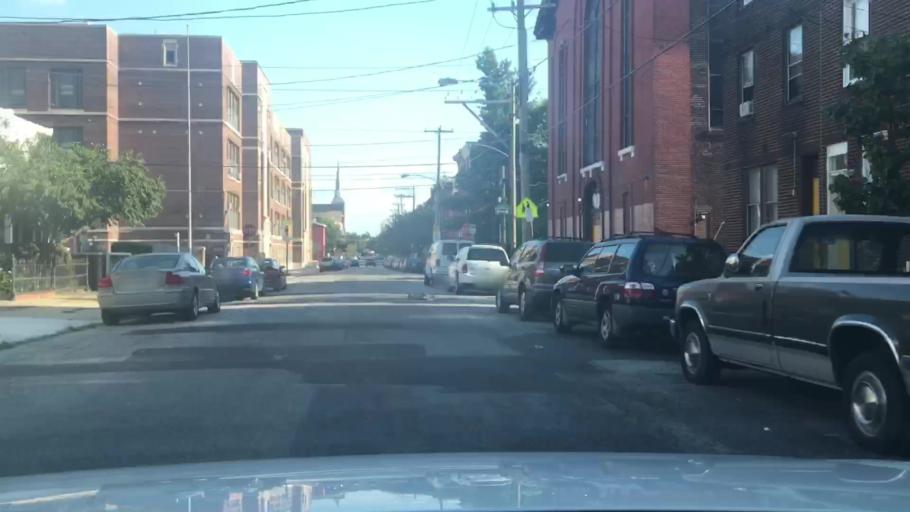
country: US
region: Pennsylvania
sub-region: Philadelphia County
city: Philadelphia
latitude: 39.9853
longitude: -75.1277
